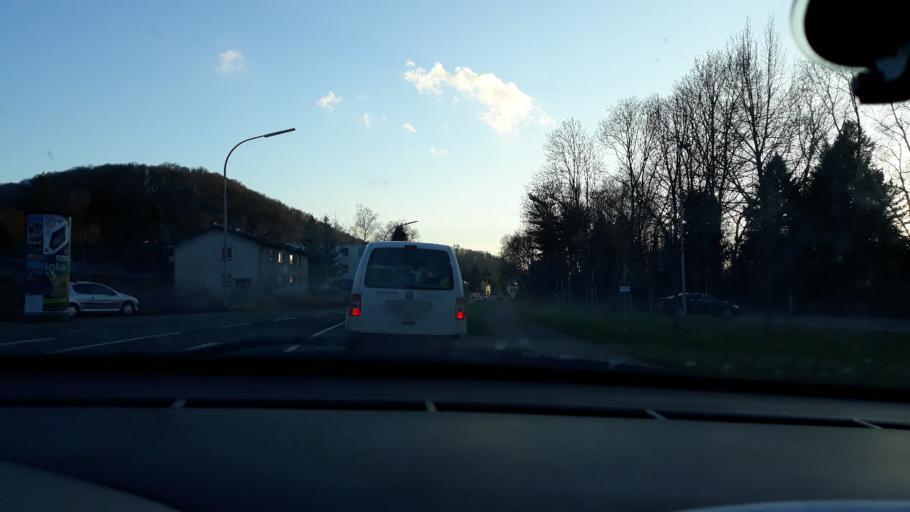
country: FR
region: Lorraine
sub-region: Departement de la Moselle
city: Spicheren
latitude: 49.2062
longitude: 6.9607
